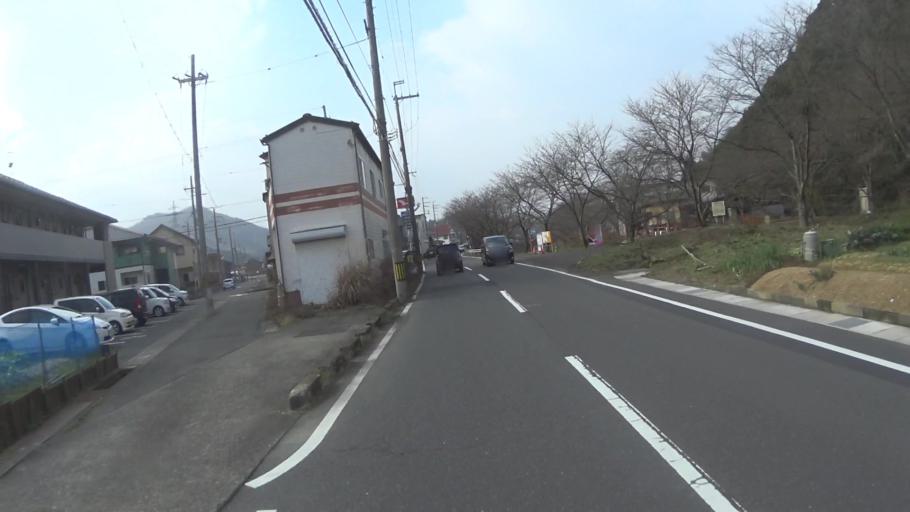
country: JP
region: Kyoto
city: Maizuru
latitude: 35.4519
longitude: 135.3998
